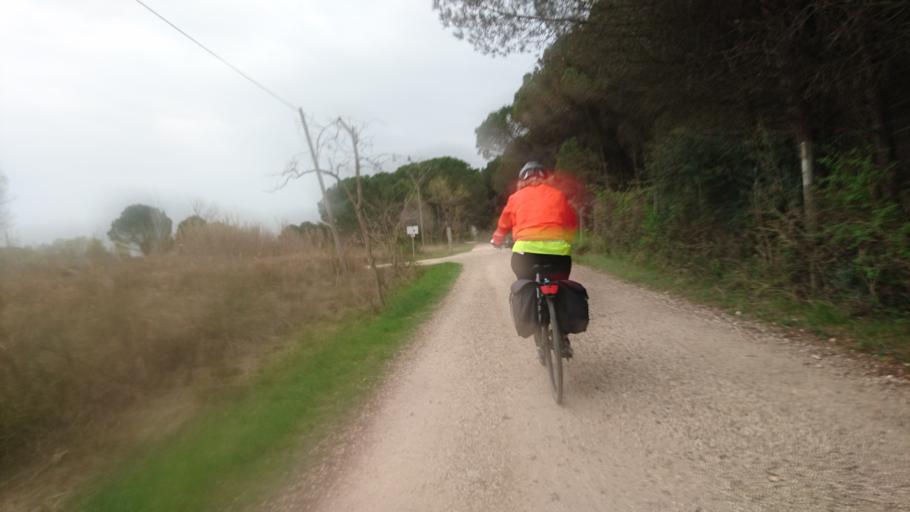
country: IT
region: Friuli Venezia Giulia
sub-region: Provincia di Udine
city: Lignano Sabbiadoro
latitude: 45.6465
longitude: 13.0933
